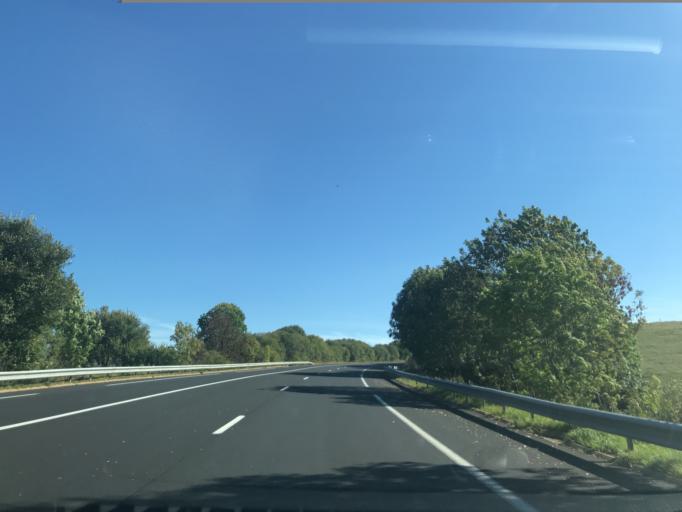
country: FR
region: Auvergne
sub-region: Departement du Puy-de-Dome
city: La Bourboule
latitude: 45.6653
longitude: 2.7387
